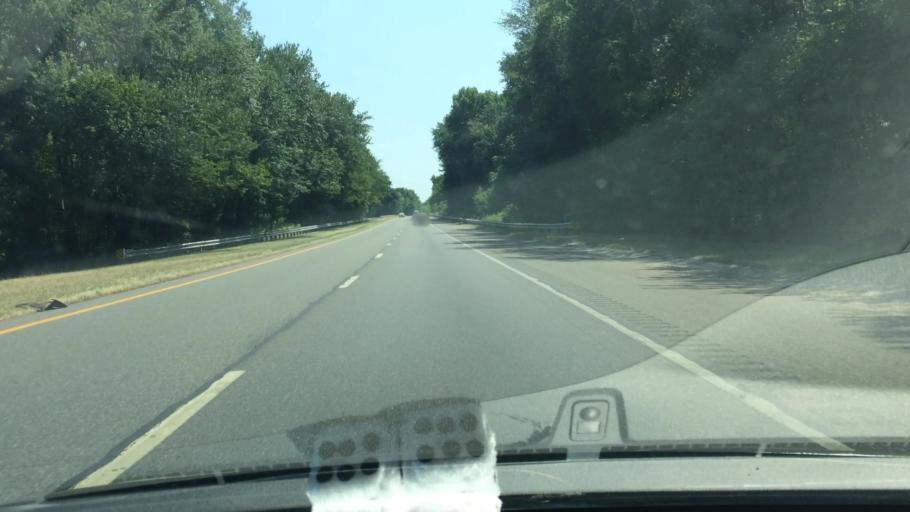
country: US
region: New Jersey
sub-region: Gloucester County
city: Beckett
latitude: 39.7862
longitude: -75.3340
